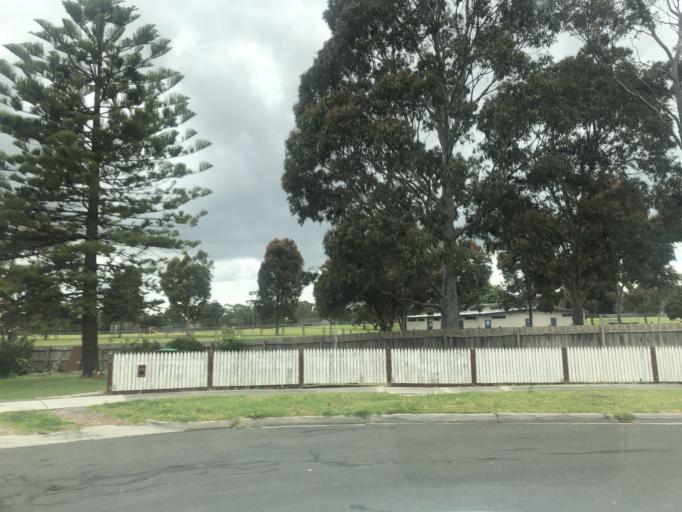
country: AU
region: Victoria
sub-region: Casey
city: Doveton
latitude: -37.9826
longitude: 145.2274
